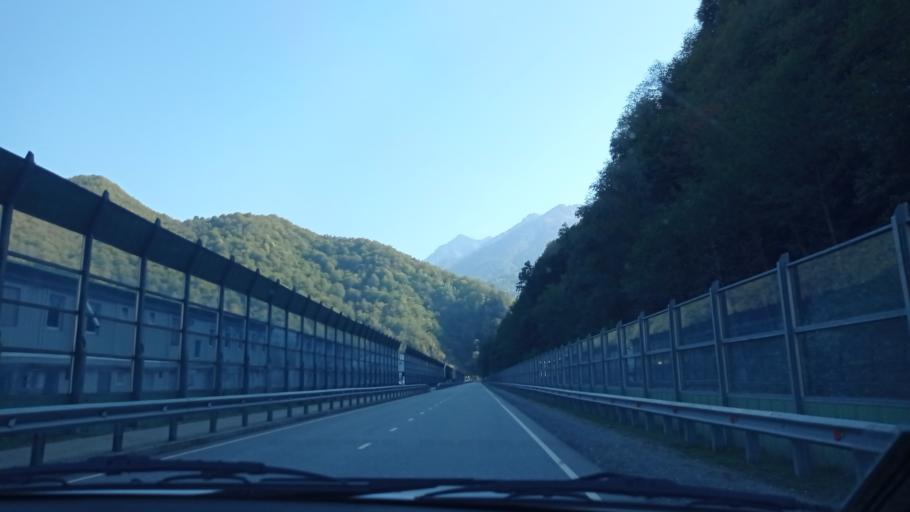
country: RU
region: Krasnodarskiy
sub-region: Sochi City
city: Krasnaya Polyana
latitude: 43.6885
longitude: 40.2746
